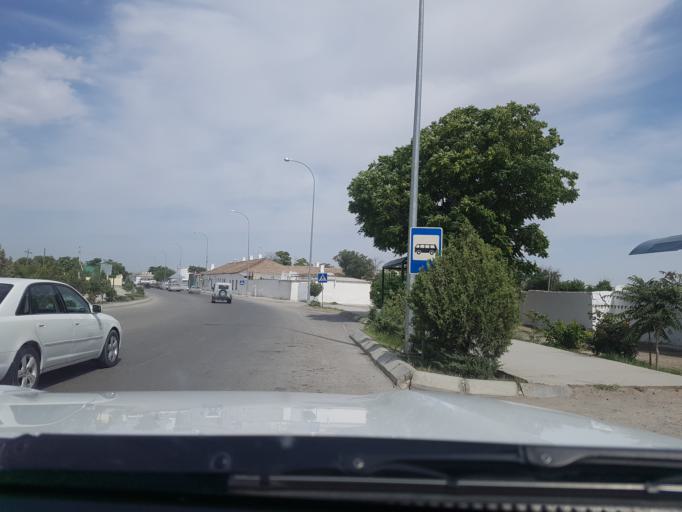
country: TM
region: Balkan
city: Serdar
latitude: 38.9825
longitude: 56.2792
